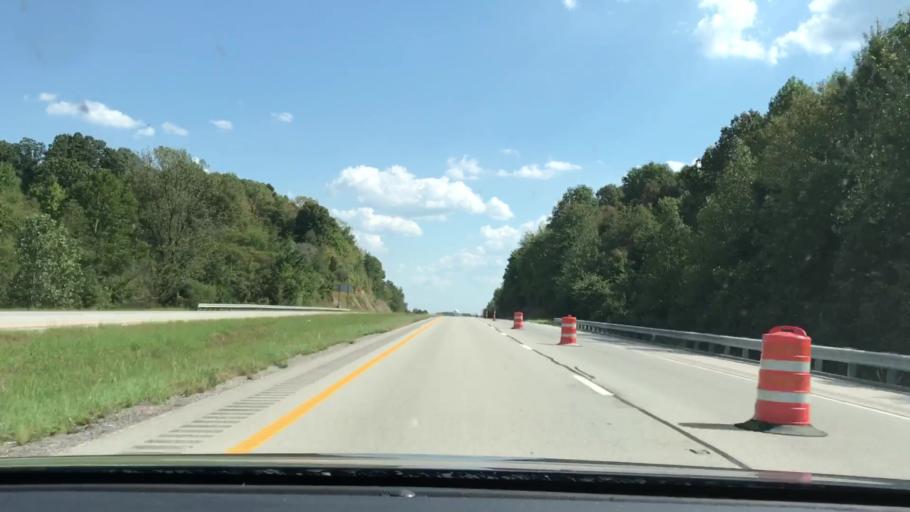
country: US
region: Kentucky
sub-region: Butler County
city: Morgantown
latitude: 37.2275
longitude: -86.7228
